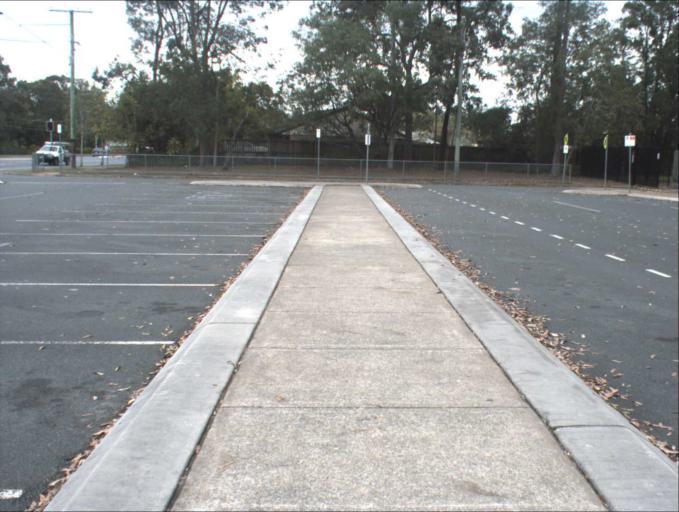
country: AU
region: Queensland
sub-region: Logan
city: Park Ridge South
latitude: -27.6840
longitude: 153.0178
